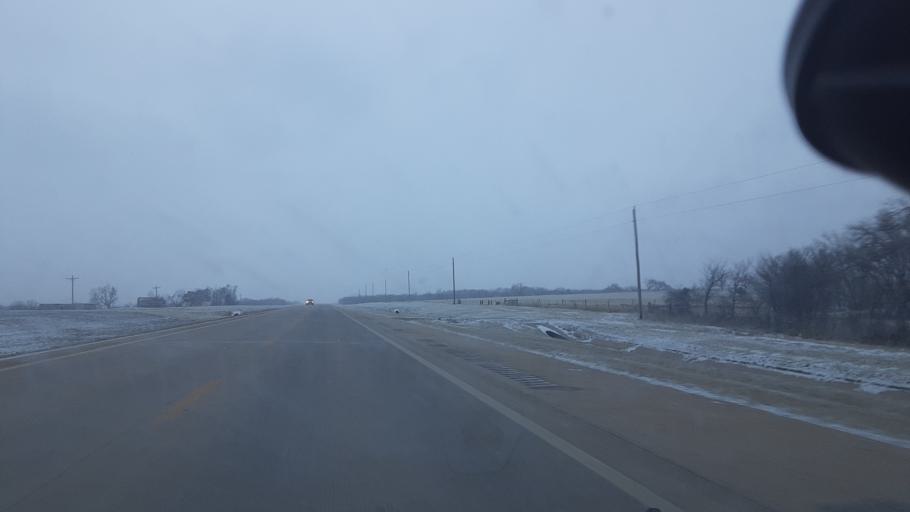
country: US
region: Oklahoma
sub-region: Payne County
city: Perkins
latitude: 35.9859
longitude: -97.1304
